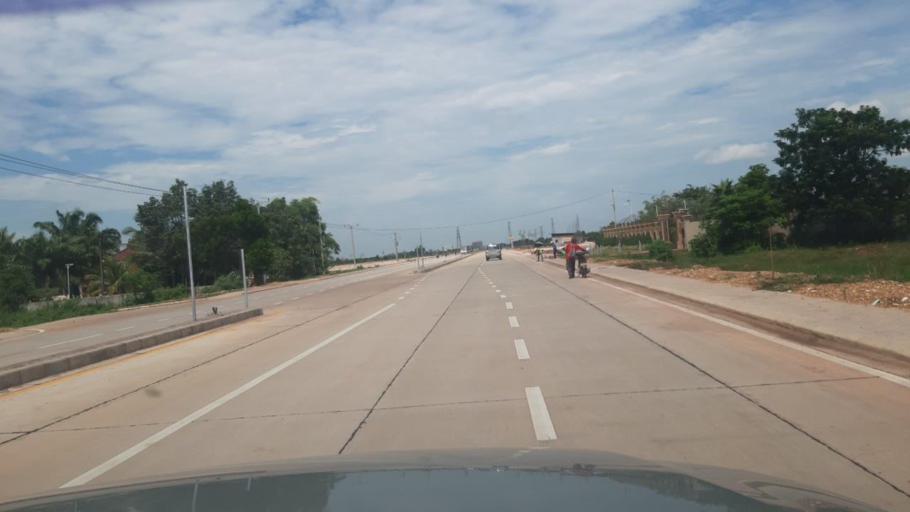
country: LA
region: Vientiane
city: Vientiane
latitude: 18.0282
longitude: 102.6057
